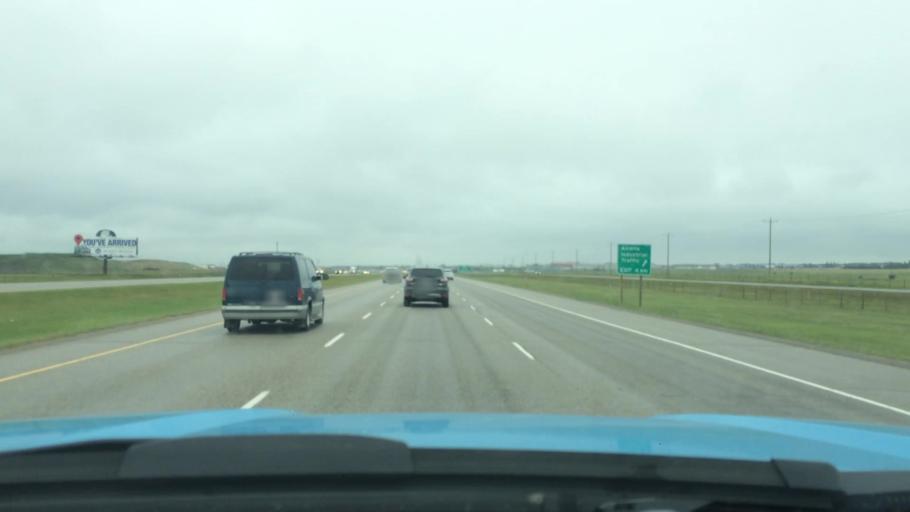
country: CA
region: Alberta
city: Airdrie
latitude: 51.2461
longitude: -114.0012
